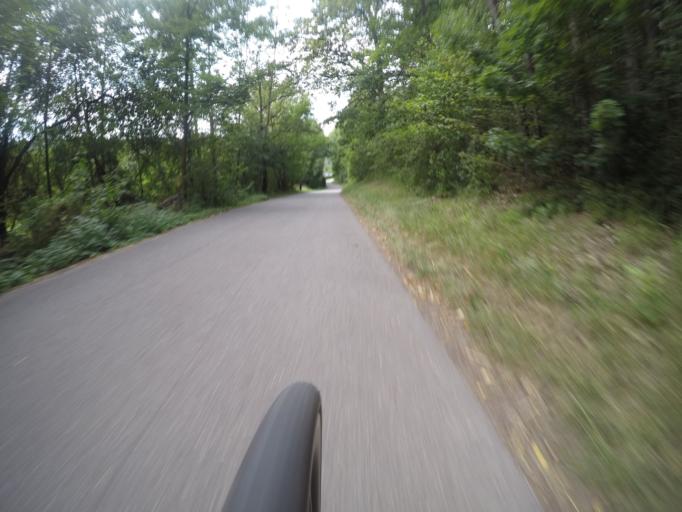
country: DE
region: Baden-Wuerttemberg
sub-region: Regierungsbezirk Stuttgart
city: Weil der Stadt
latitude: 48.7385
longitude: 8.8805
